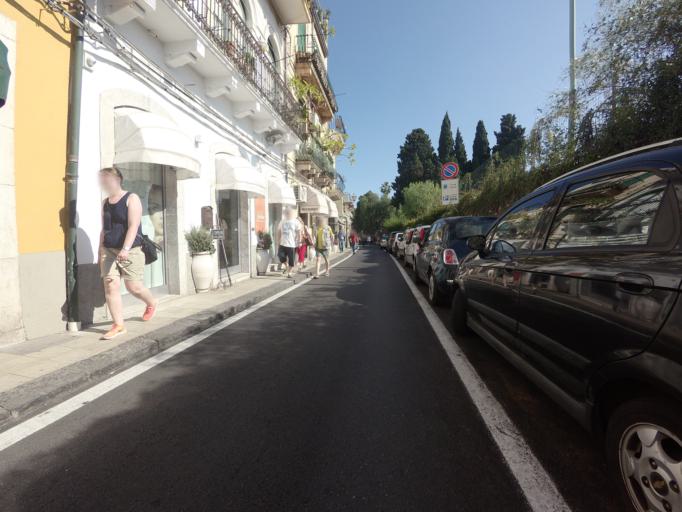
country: IT
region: Sicily
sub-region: Messina
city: Taormina
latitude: 37.8516
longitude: 15.2894
